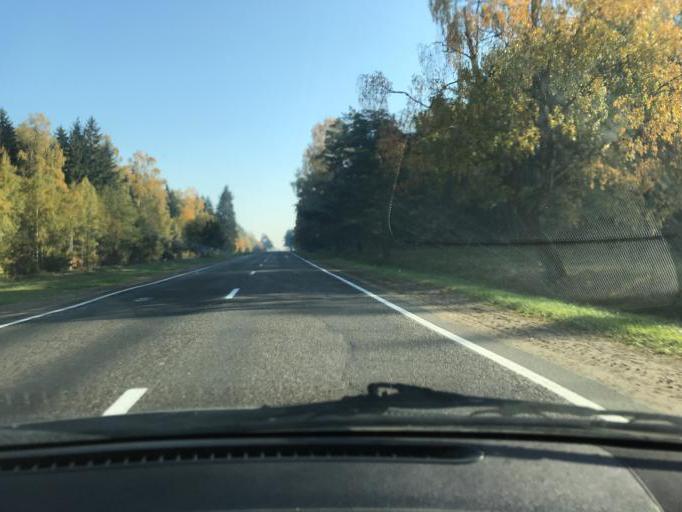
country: BY
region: Minsk
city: Klyetsk
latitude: 52.9695
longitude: 26.6294
